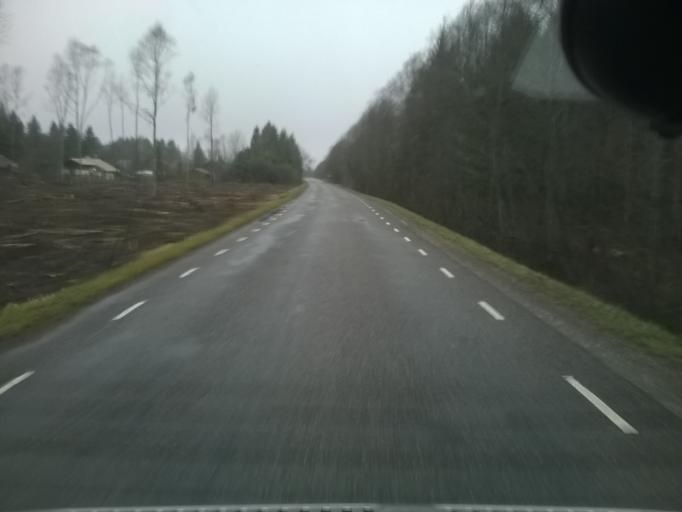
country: EE
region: Raplamaa
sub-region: Kohila vald
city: Kohila
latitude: 59.2032
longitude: 24.6680
